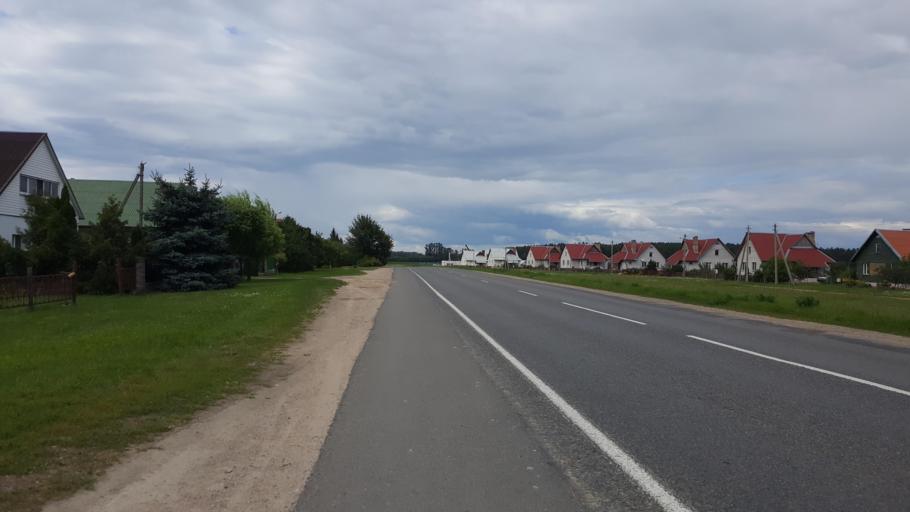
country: BY
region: Brest
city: Kamyanyets
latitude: 52.3262
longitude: 23.9169
